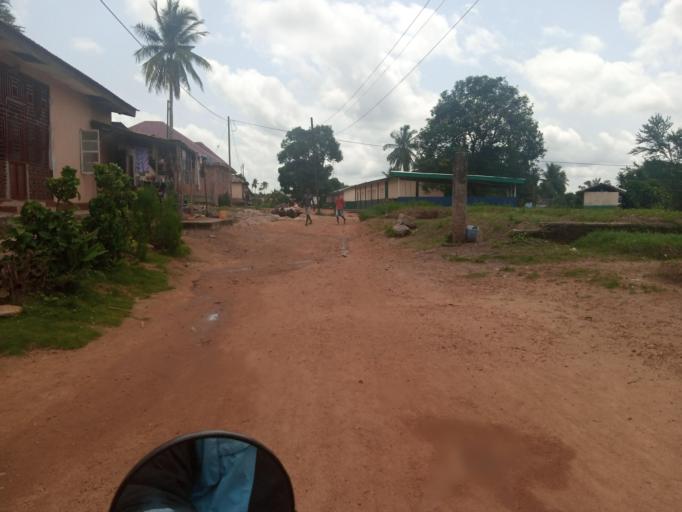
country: SL
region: Southern Province
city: Bo
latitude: 7.9535
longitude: -11.7404
